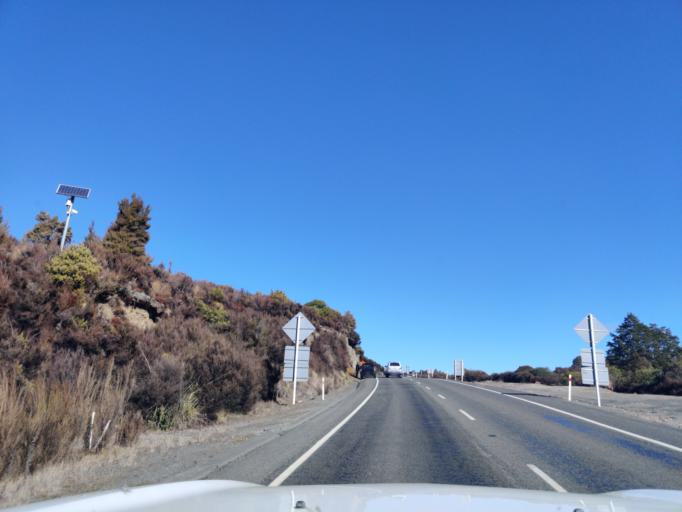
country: NZ
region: Waikato
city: Turangi
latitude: -39.2175
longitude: 175.7358
